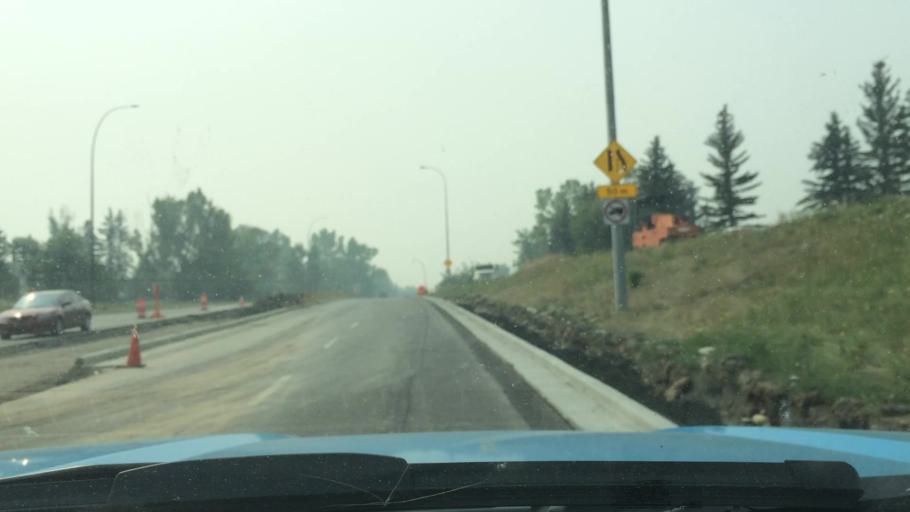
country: CA
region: Alberta
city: Calgary
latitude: 50.9497
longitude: -114.0949
